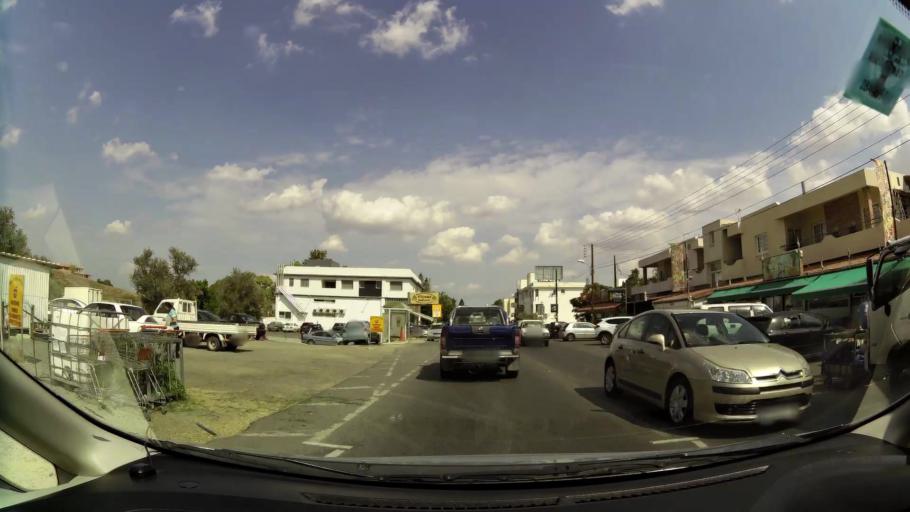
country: CY
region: Lefkosia
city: Tseri
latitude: 35.0811
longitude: 33.3271
